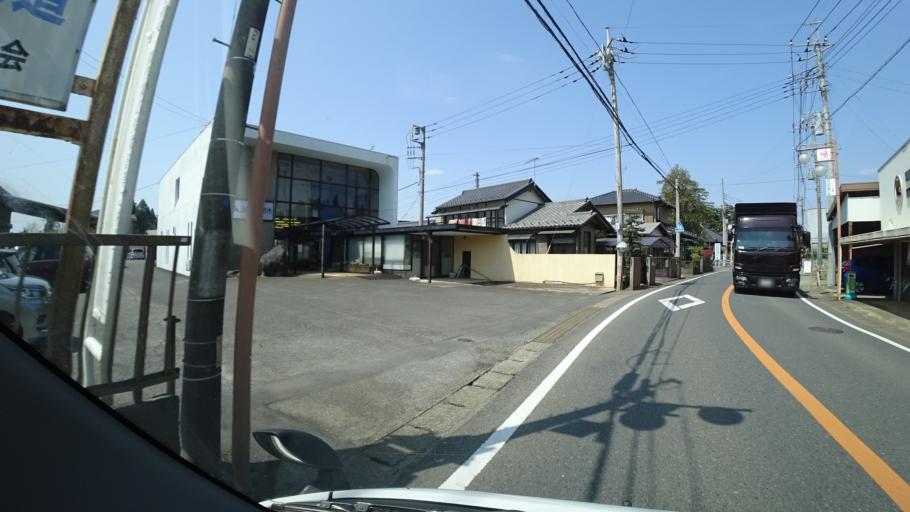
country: JP
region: Chiba
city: Naruto
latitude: 35.6927
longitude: 140.4159
